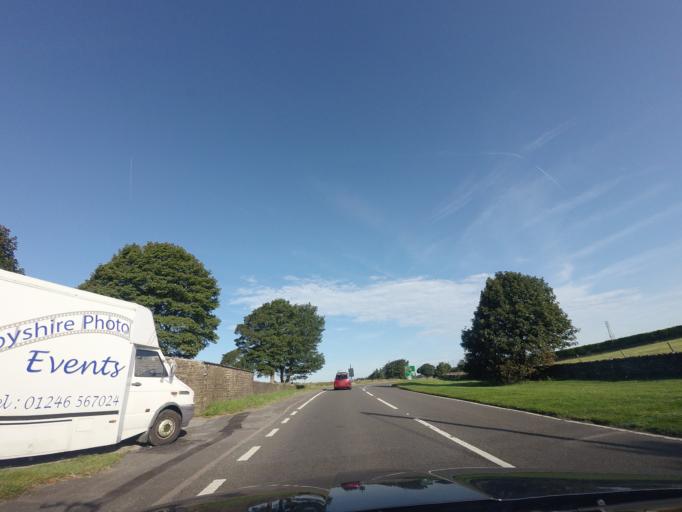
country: GB
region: England
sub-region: Derbyshire
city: Dronfield
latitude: 53.2356
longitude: -1.5345
